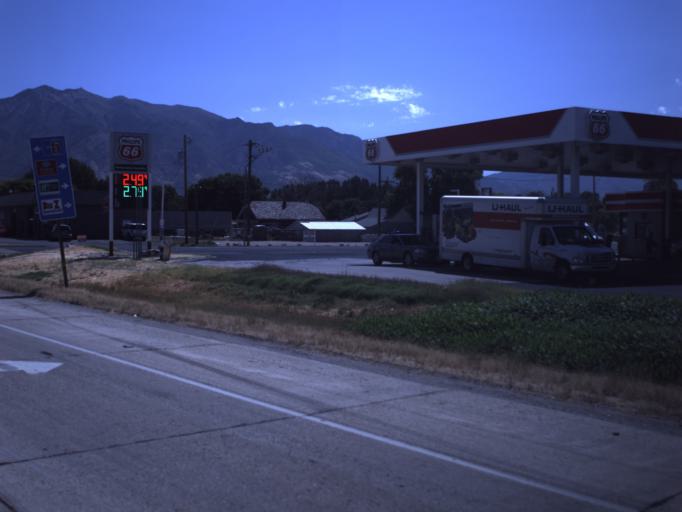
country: US
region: Utah
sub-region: Weber County
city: Marriott-Slaterville
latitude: 41.2292
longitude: -112.0073
